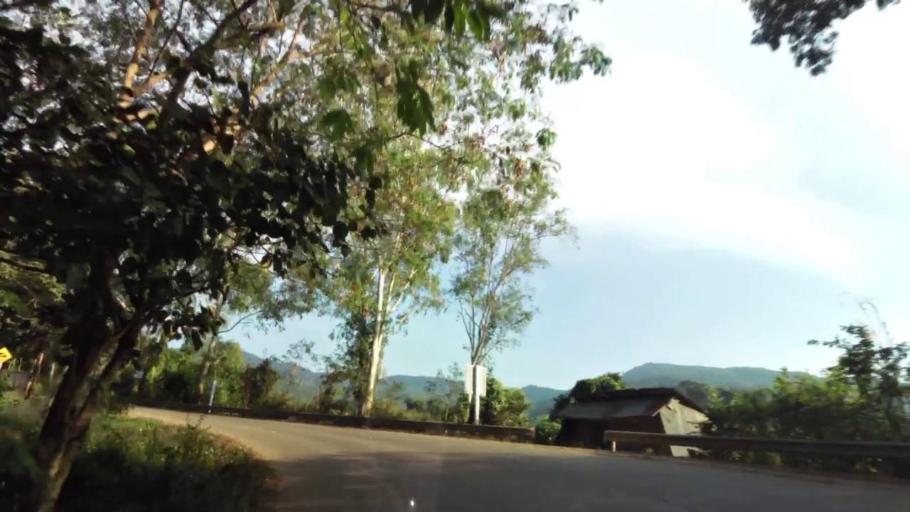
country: TH
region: Chiang Rai
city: Khun Tan
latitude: 19.8675
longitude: 100.4013
